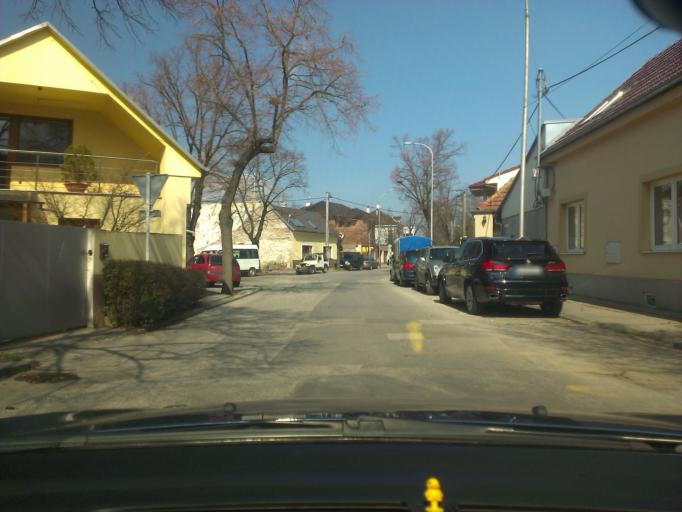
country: SK
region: Trnavsky
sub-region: Okres Trnava
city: Piestany
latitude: 48.5956
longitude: 17.8323
